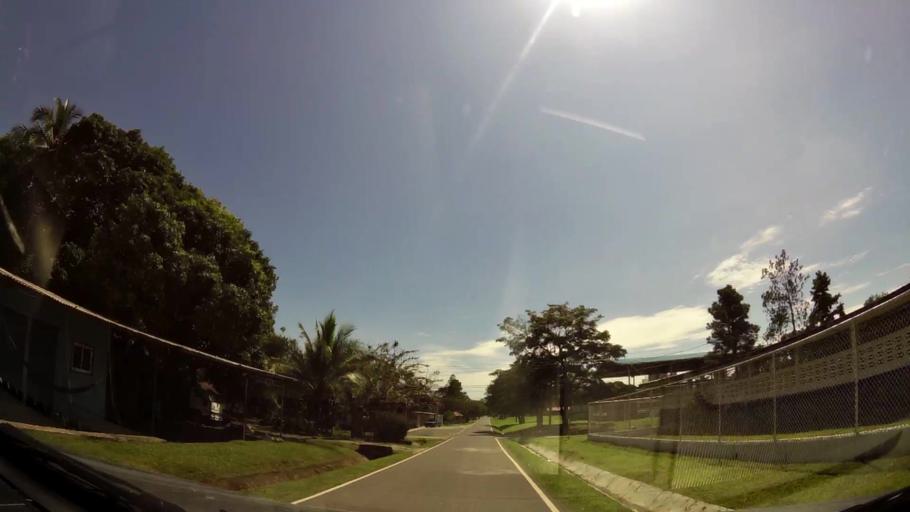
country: PA
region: Panama
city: Nueva Gorgona
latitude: 8.5539
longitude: -79.8730
